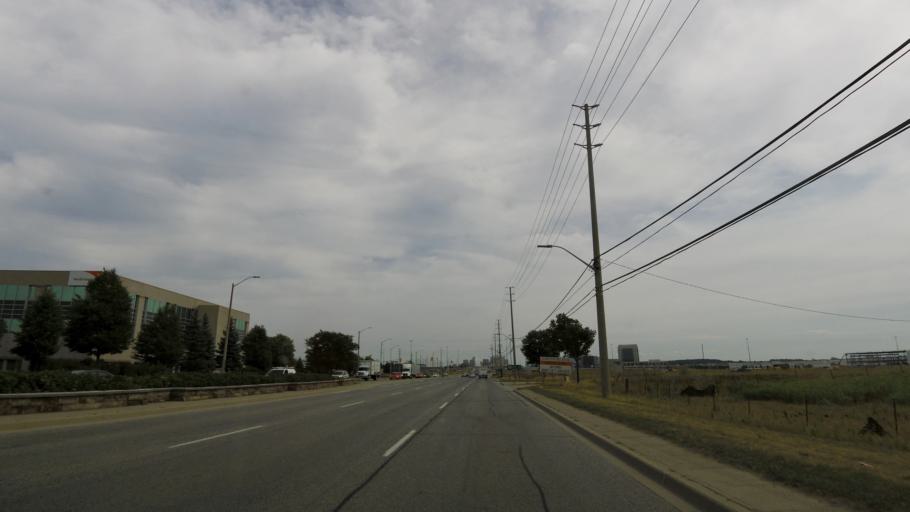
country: CA
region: Ontario
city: Mississauga
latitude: 43.6346
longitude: -79.6910
